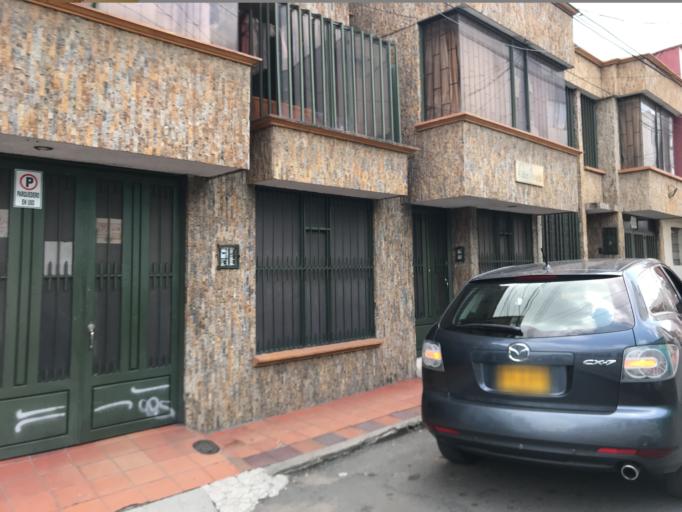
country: CO
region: Boyaca
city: Tunja
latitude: 5.5368
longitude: -73.3576
